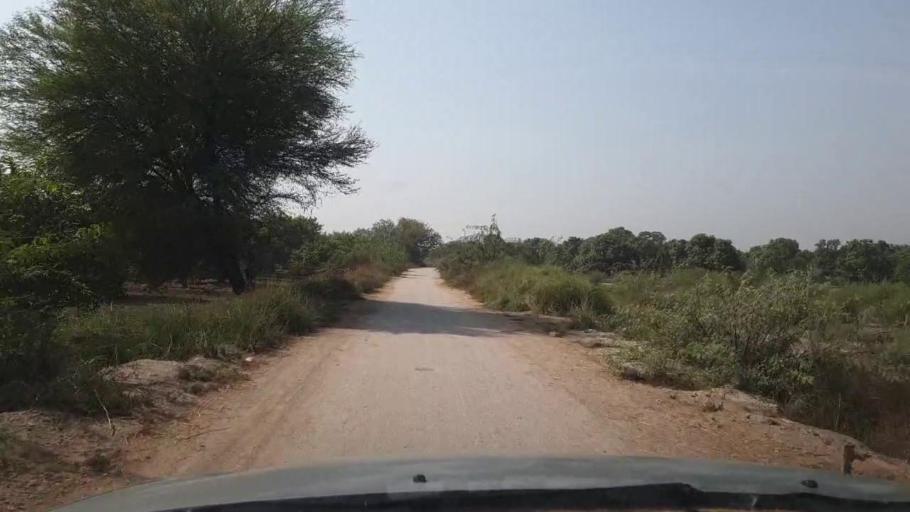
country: PK
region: Sindh
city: Tando Jam
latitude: 25.3675
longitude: 68.5299
